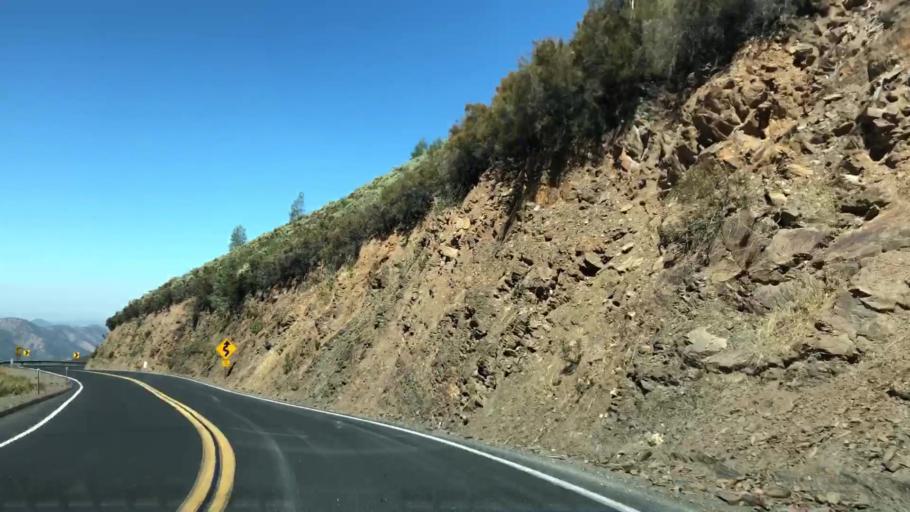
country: US
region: California
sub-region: Tuolumne County
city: Tuolumne City
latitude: 37.8181
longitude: -120.2723
